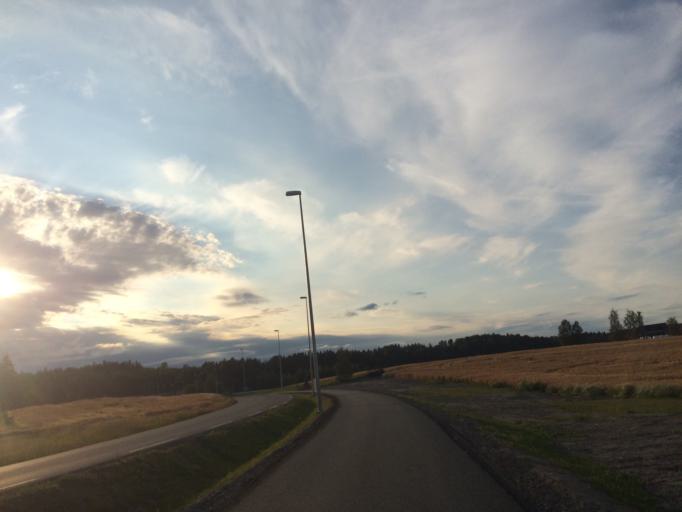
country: NO
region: Akershus
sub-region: Ski
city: Ski
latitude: 59.6956
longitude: 10.8581
